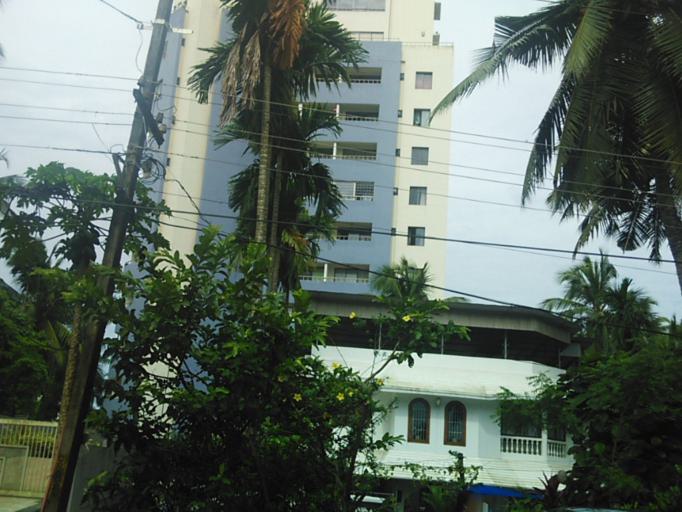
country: IN
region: Kerala
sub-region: Kozhikode
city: Kozhikode
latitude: 11.2807
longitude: 75.8068
